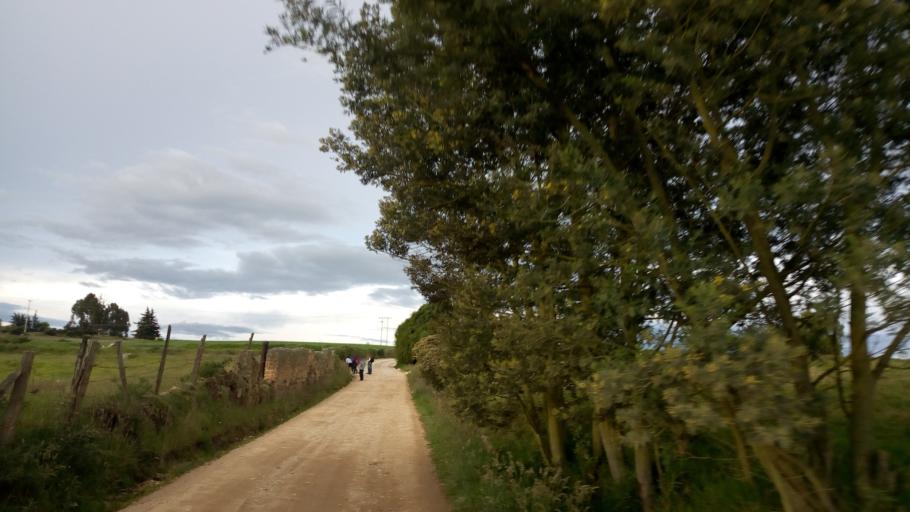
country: CO
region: Boyaca
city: Toca
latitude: 5.5827
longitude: -73.1733
